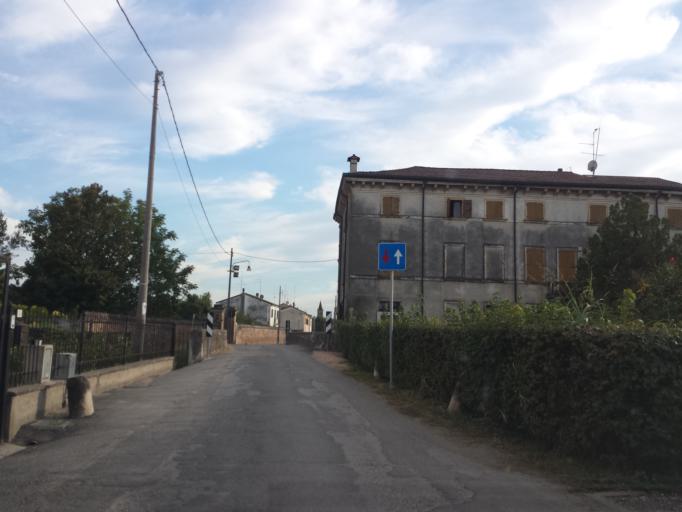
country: IT
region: Veneto
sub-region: Provincia di Verona
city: Isola della Scala
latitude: 45.2745
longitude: 10.9989
